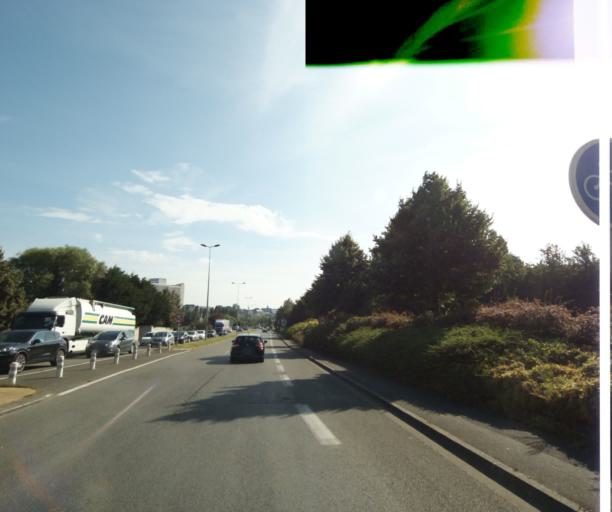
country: FR
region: Pays de la Loire
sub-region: Departement de la Mayenne
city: Laval
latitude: 48.0592
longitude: -0.7871
